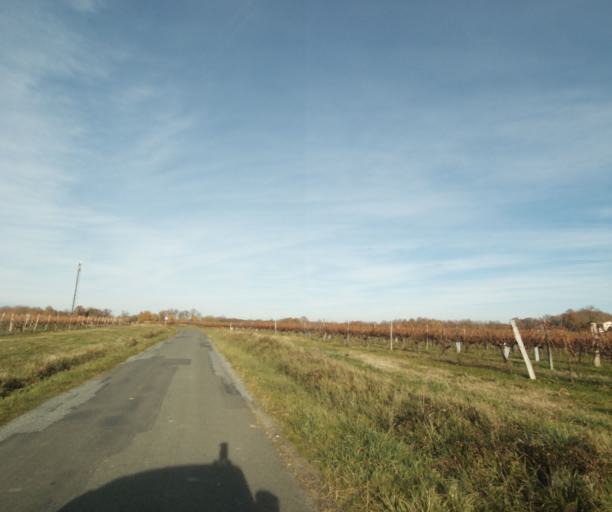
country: FR
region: Poitou-Charentes
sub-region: Departement de la Charente-Maritime
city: Chaniers
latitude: 45.7413
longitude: -0.5209
